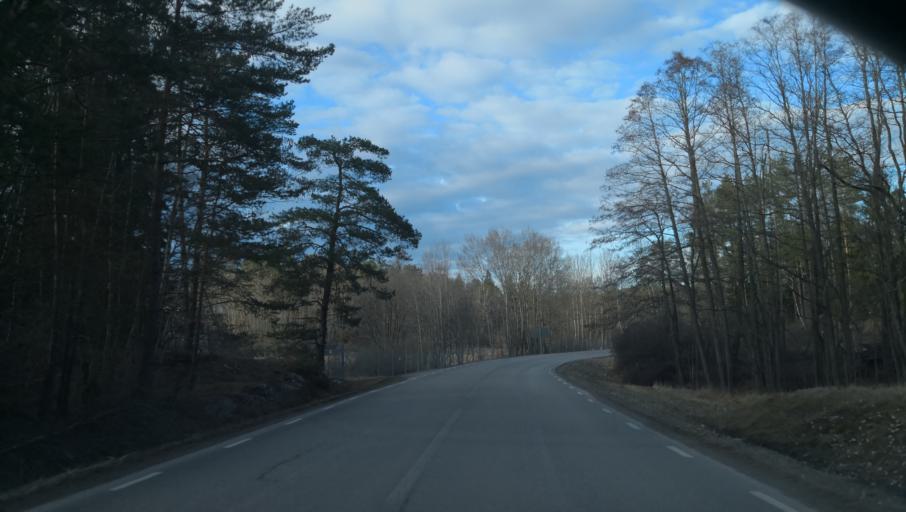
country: SE
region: Stockholm
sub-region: Varmdo Kommun
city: Gustavsberg
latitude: 59.3466
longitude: 18.3618
